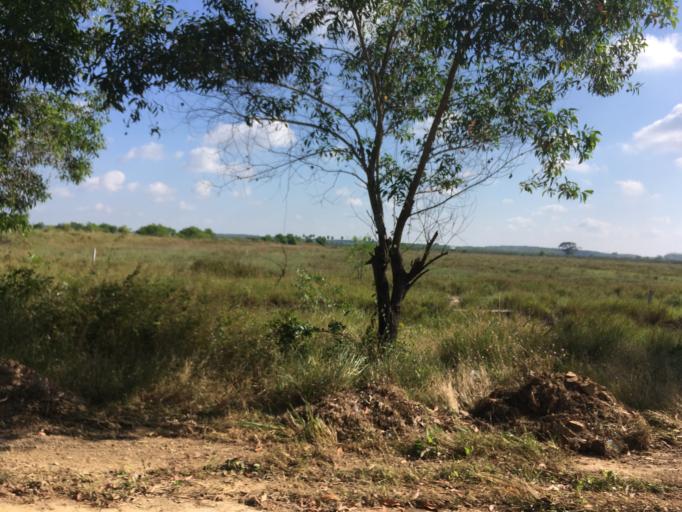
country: MM
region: Mon
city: Martaban
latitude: 16.6046
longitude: 97.7180
